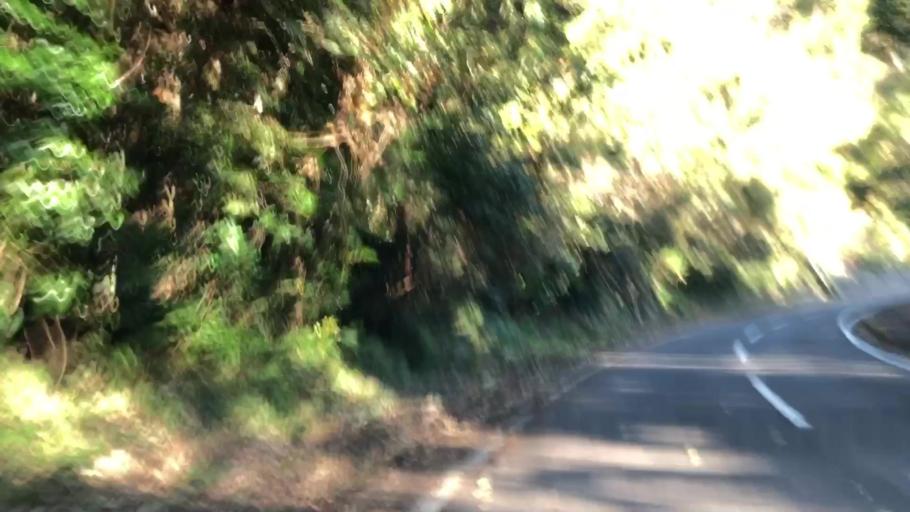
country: JP
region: Nagasaki
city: Sasebo
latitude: 33.0275
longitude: 129.6635
